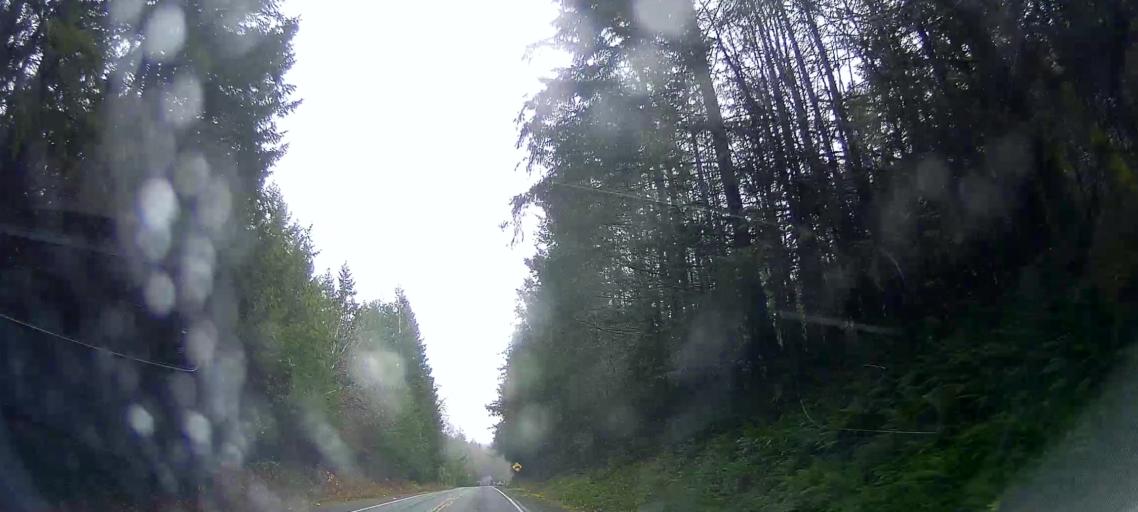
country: US
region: Washington
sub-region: Snohomish County
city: Darrington
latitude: 48.5314
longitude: -121.8001
